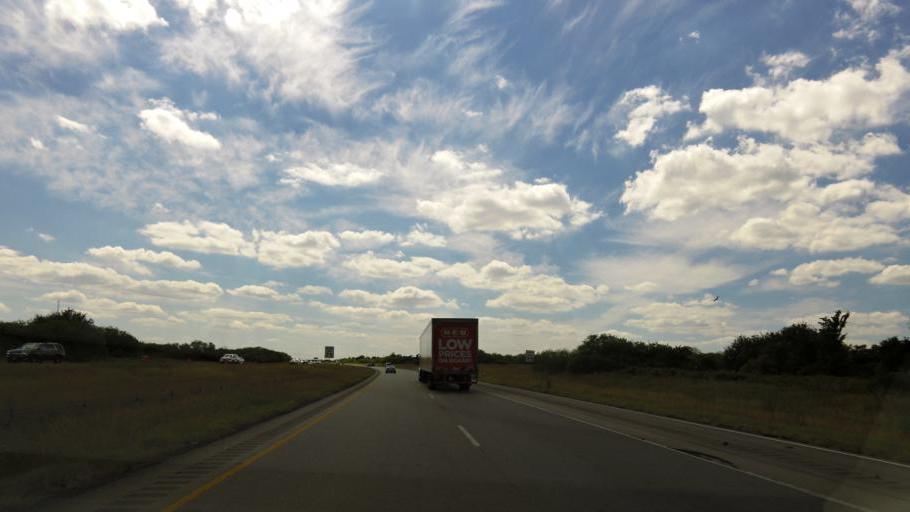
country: US
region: Texas
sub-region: Gonzales County
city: Waelder
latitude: 29.6926
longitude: -97.2403
